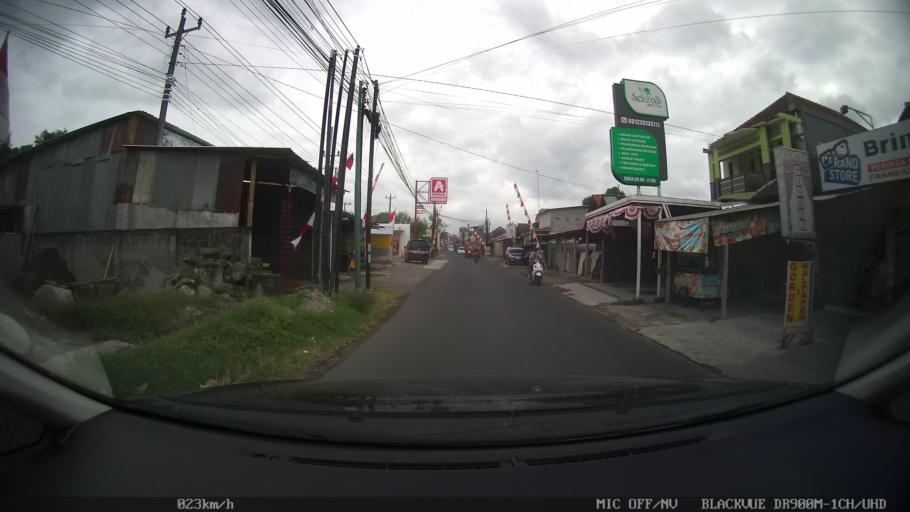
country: ID
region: Daerah Istimewa Yogyakarta
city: Sewon
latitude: -7.8336
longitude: 110.4124
